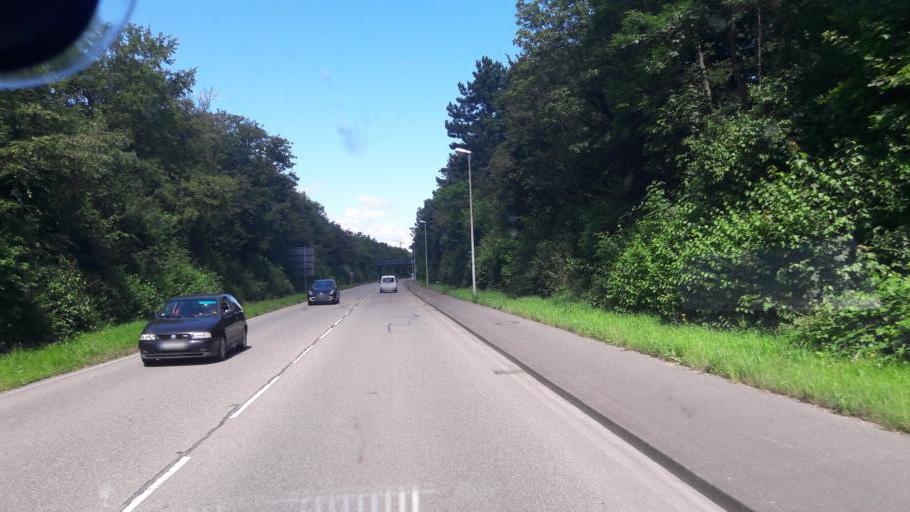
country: DE
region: Baden-Wuerttemberg
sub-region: Karlsruhe Region
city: Bruchsal
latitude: 49.1190
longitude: 8.5667
